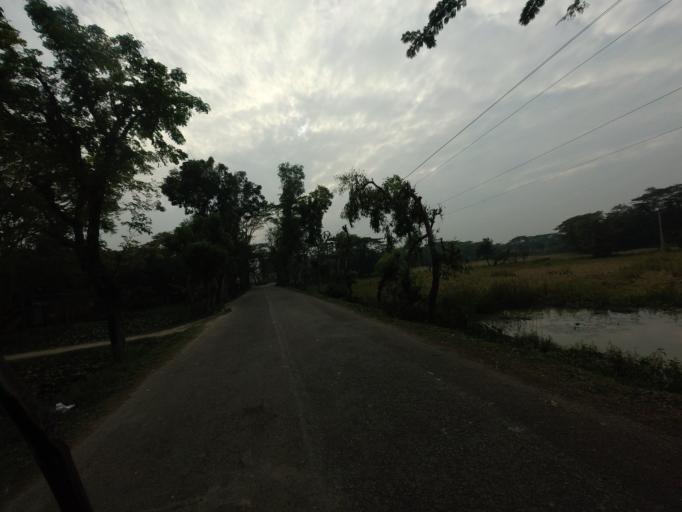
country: BD
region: Barisal
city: Nalchiti
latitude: 22.4561
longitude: 90.3505
